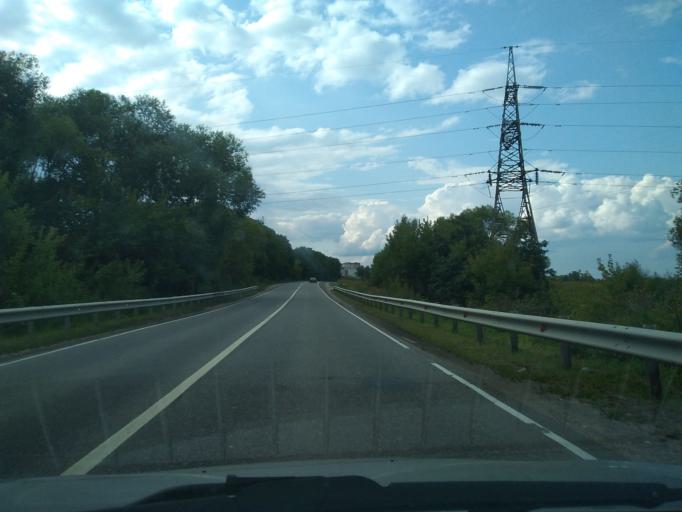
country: RU
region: Moskovskaya
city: Voskresensk
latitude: 55.2989
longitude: 38.6645
